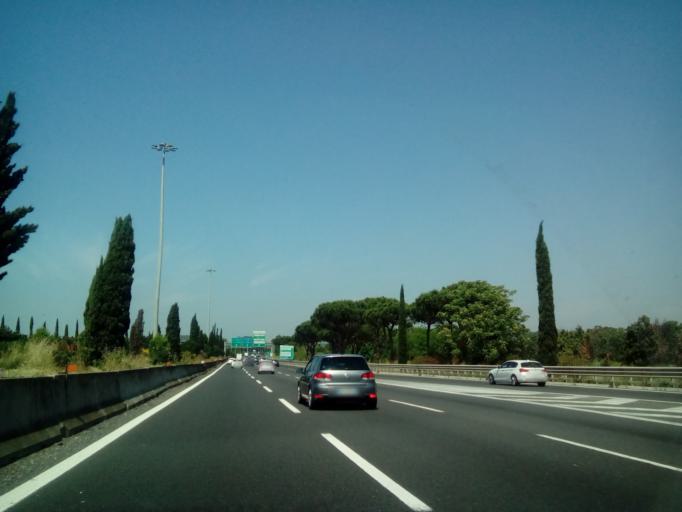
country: IT
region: Latium
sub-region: Citta metropolitana di Roma Capitale
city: Vitinia
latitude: 41.8088
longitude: 12.4120
